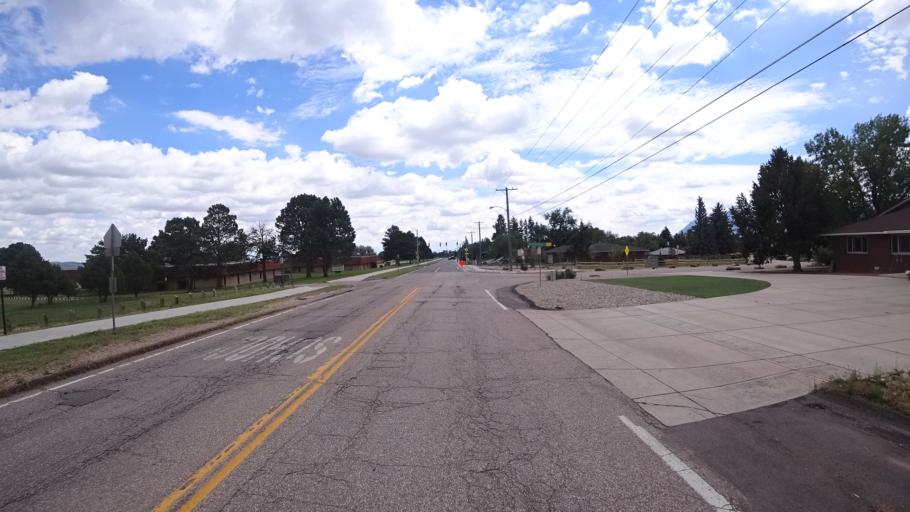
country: US
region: Colorado
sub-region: El Paso County
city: Colorado Springs
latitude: 38.8682
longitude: -104.8582
